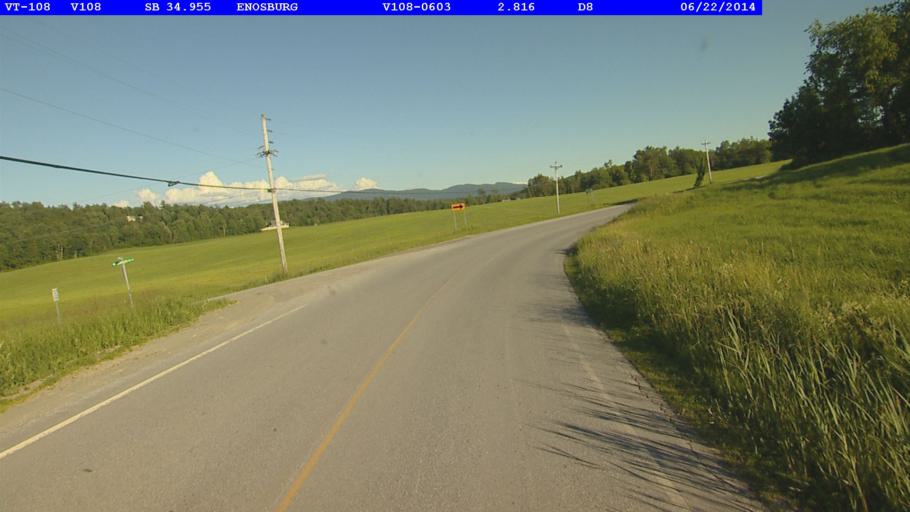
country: US
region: Vermont
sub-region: Franklin County
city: Enosburg Falls
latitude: 44.8775
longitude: -72.7953
